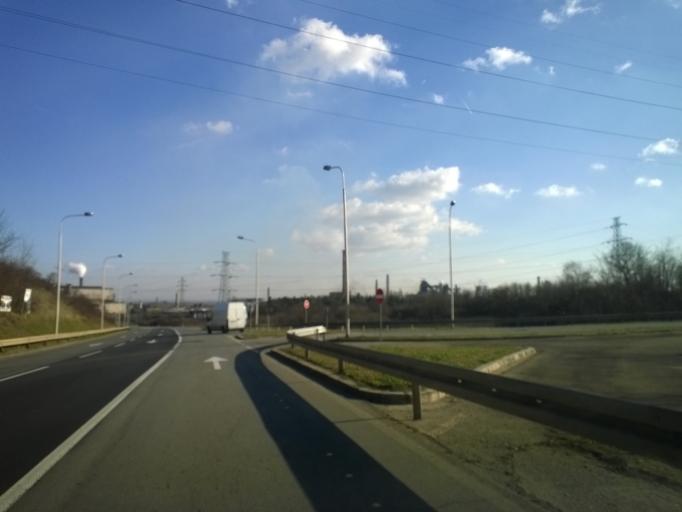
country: RS
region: Central Serbia
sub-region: Podunavski Okrug
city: Smederevo
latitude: 44.6095
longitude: 20.9560
